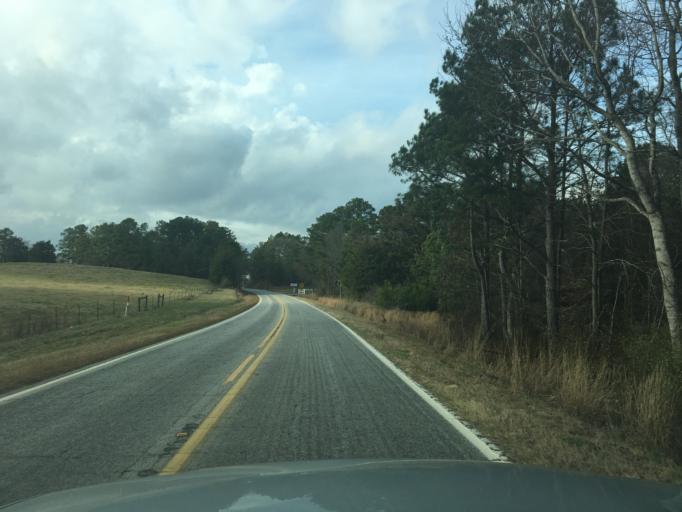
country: US
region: South Carolina
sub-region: Abbeville County
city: Abbeville
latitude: 34.2358
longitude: -82.3946
